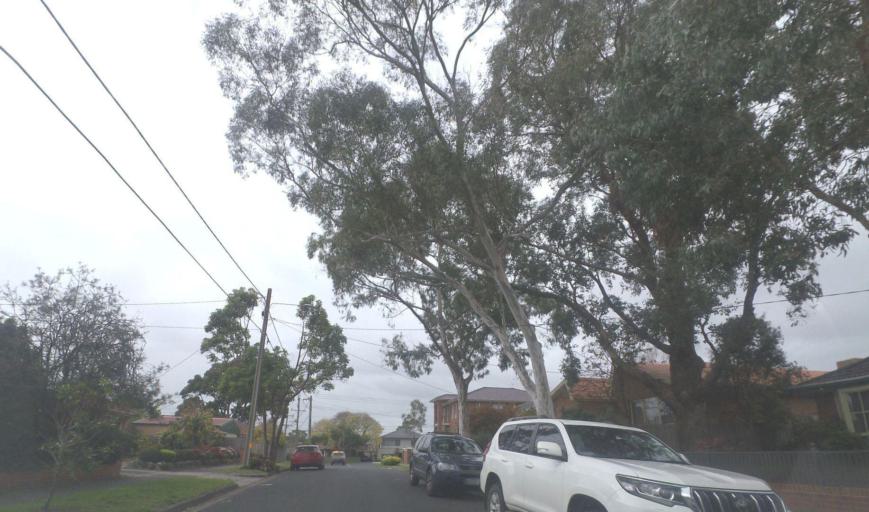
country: AU
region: Victoria
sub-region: Whitehorse
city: Blackburn North
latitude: -37.8052
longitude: 145.1521
